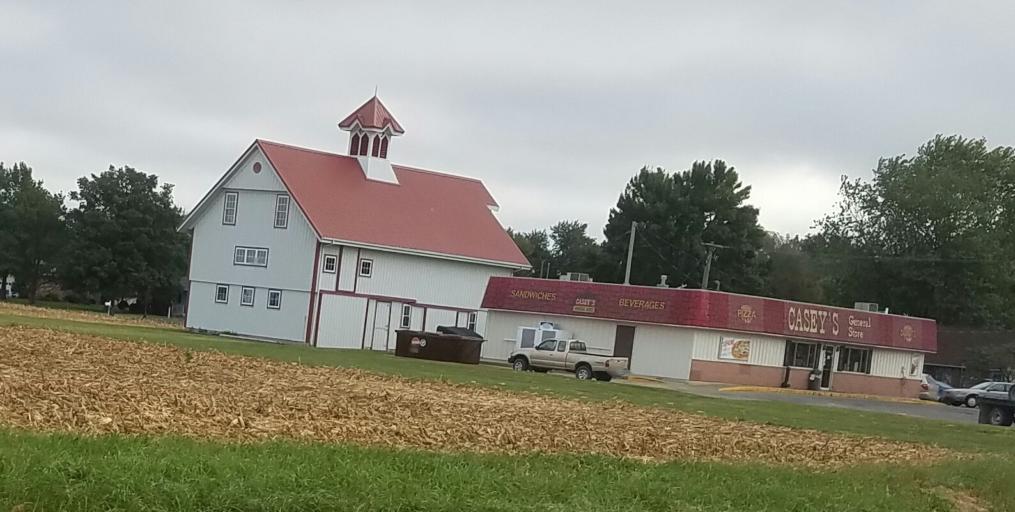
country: US
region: Illinois
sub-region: Hancock County
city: Carthage
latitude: 40.4159
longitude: -91.1447
